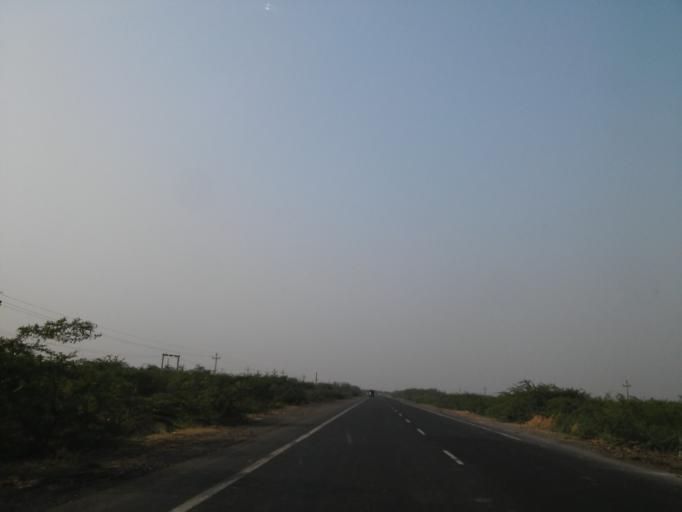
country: IN
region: Gujarat
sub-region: Kachchh
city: Anjar
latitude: 23.2964
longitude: 70.1000
